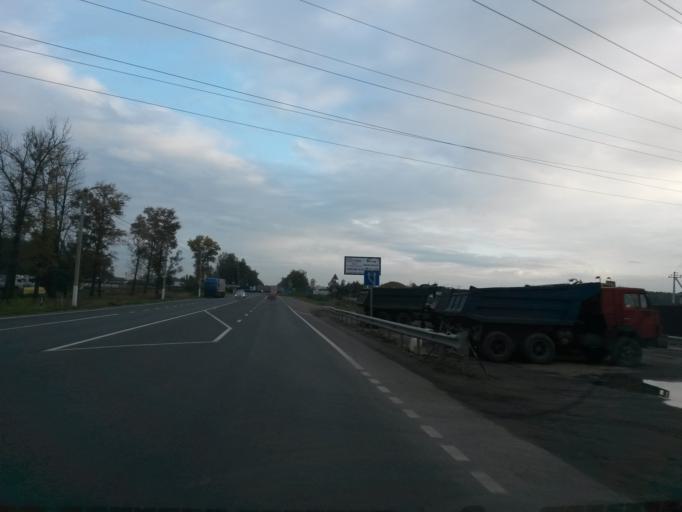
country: RU
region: Moskovskaya
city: L'vovskiy
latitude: 55.3302
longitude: 37.5285
